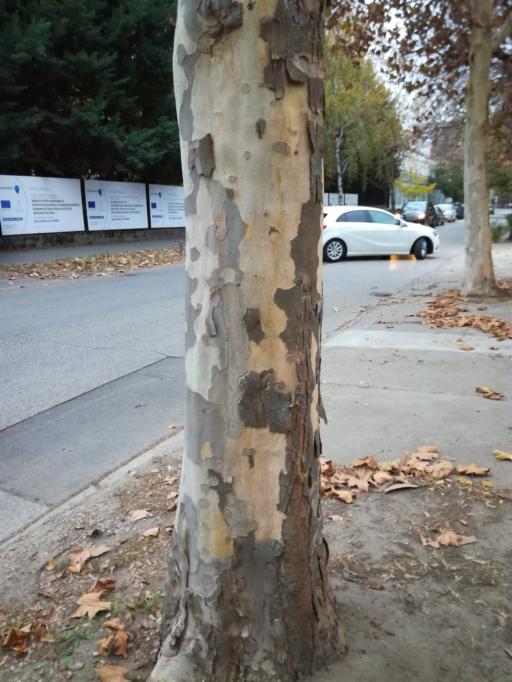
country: HU
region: Csongrad
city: Szeged
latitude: 46.2442
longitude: 20.1661
